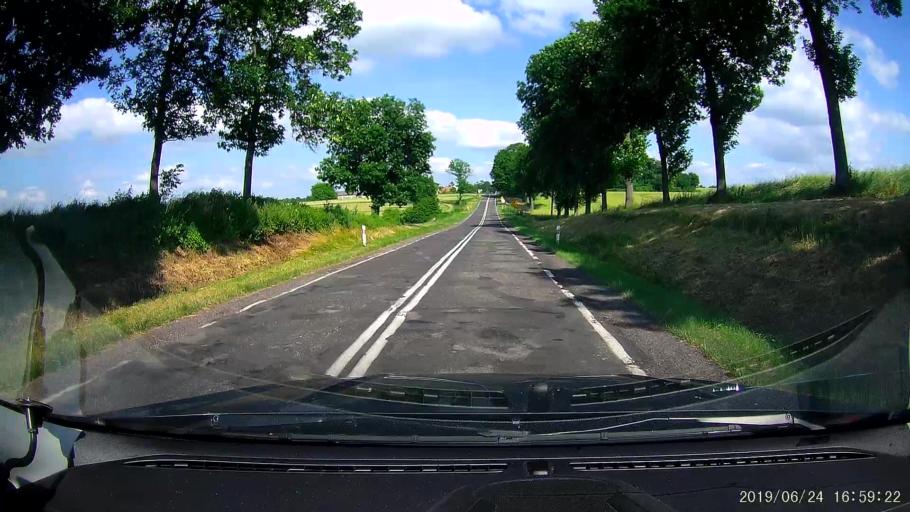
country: PL
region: Lublin Voivodeship
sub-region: Powiat tomaszowski
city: Telatyn
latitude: 50.5236
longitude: 23.9007
